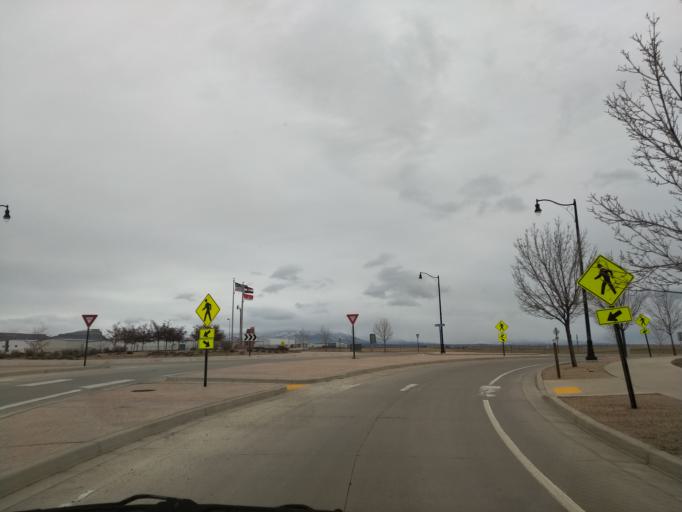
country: US
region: Colorado
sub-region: Mesa County
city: Fruitvale
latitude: 39.1183
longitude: -108.5305
